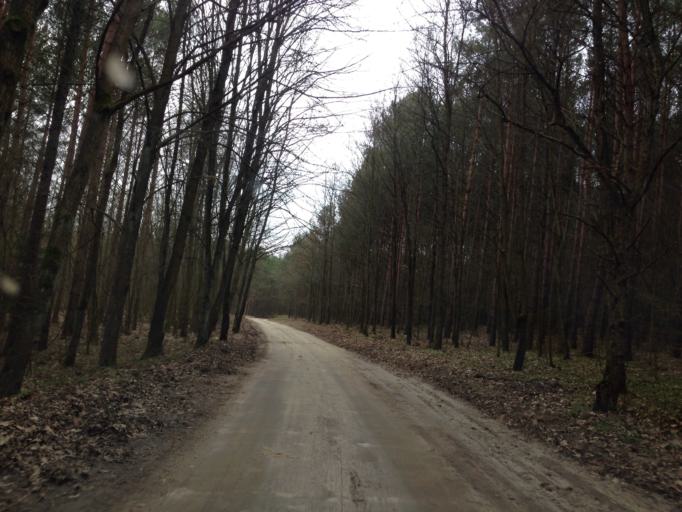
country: PL
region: Warmian-Masurian Voivodeship
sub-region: Powiat dzialdowski
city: Lidzbark
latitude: 53.2172
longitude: 19.7426
